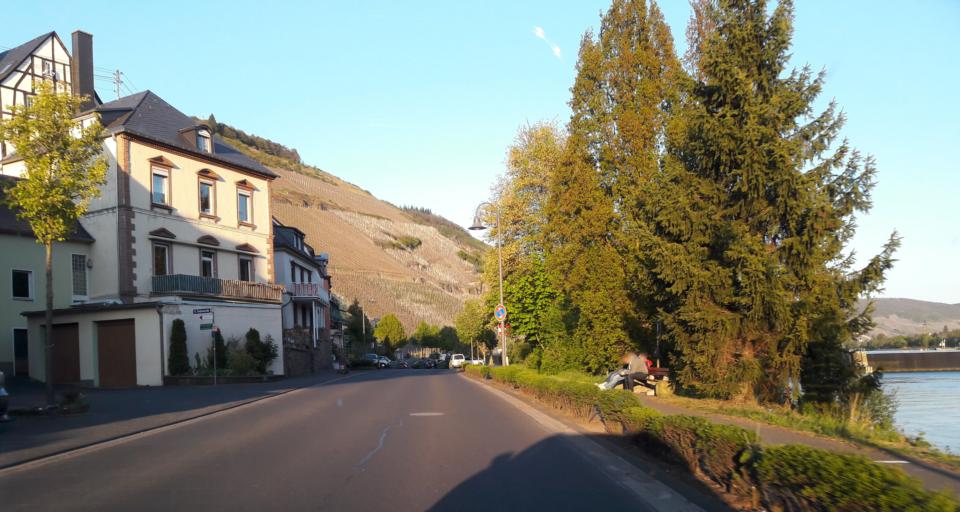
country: DE
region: Rheinland-Pfalz
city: Zeltingen-Rachtig
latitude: 49.9519
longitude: 7.0194
